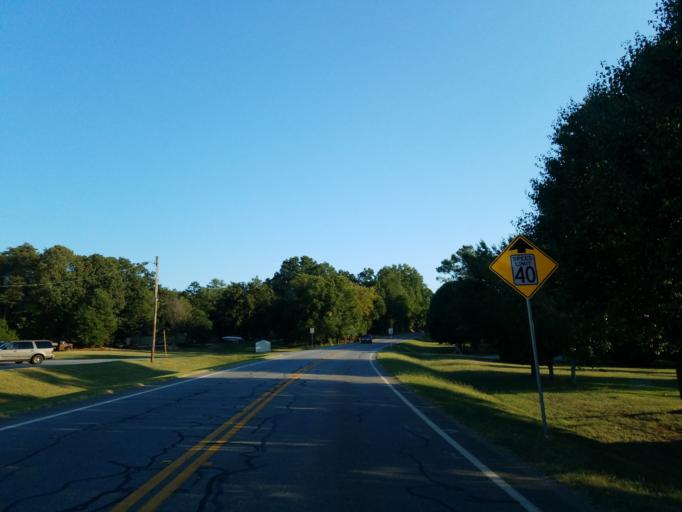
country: US
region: Georgia
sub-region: Bartow County
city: Rydal
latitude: 34.4435
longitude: -84.7008
